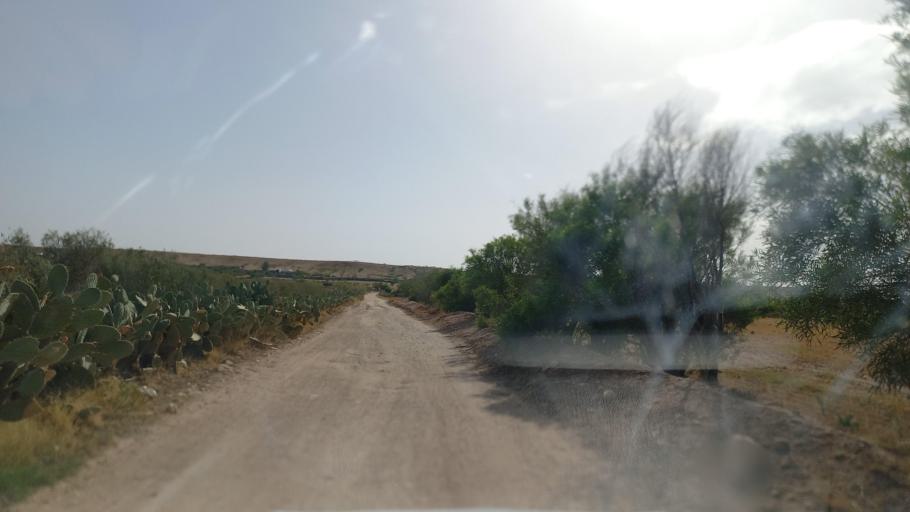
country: TN
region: Al Qasrayn
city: Kasserine
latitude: 35.2651
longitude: 8.9328
